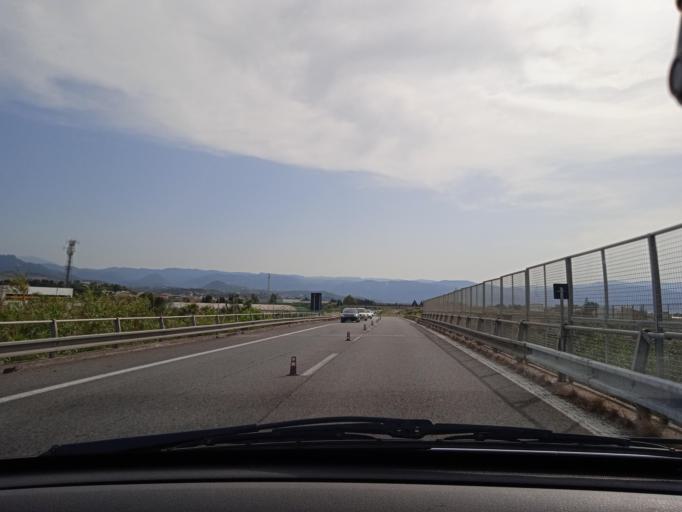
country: IT
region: Sicily
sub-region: Messina
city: Terme
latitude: 38.1485
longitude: 15.1731
